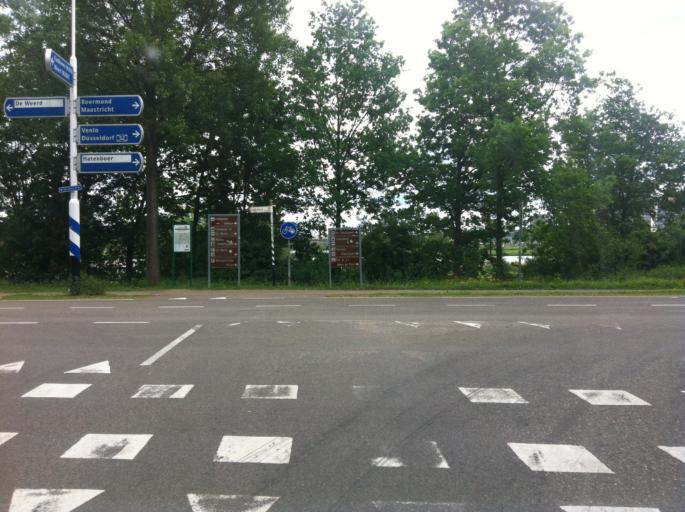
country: NL
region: Limburg
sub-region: Gemeente Roermond
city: Roermond
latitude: 51.2010
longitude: 5.9764
